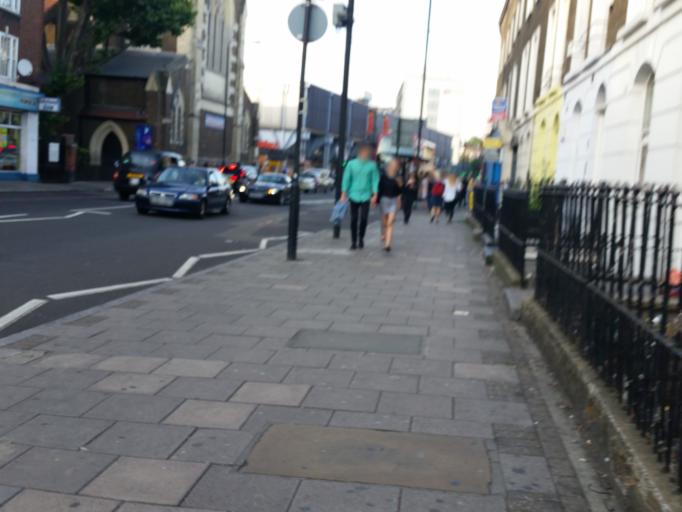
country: GB
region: England
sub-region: Greater London
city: Camden Town
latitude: 51.5395
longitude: -0.1417
